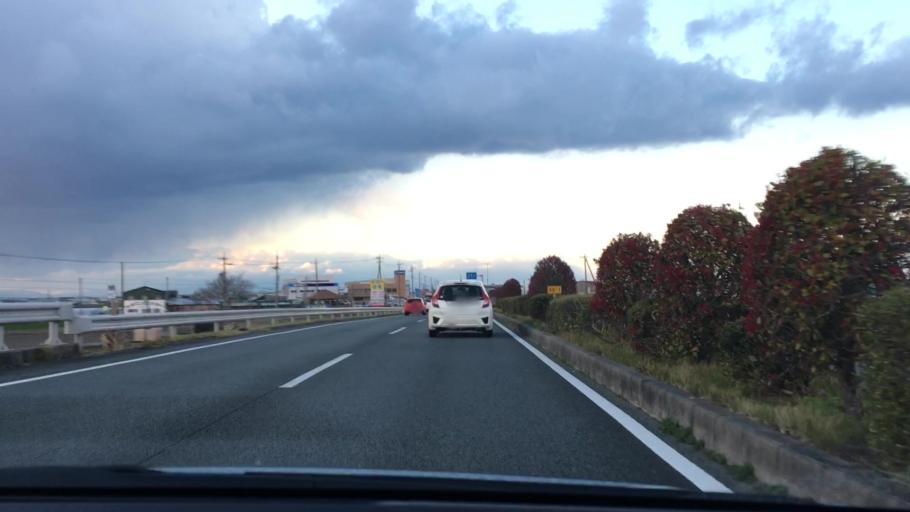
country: JP
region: Mie
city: Ise
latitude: 34.5230
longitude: 136.6846
